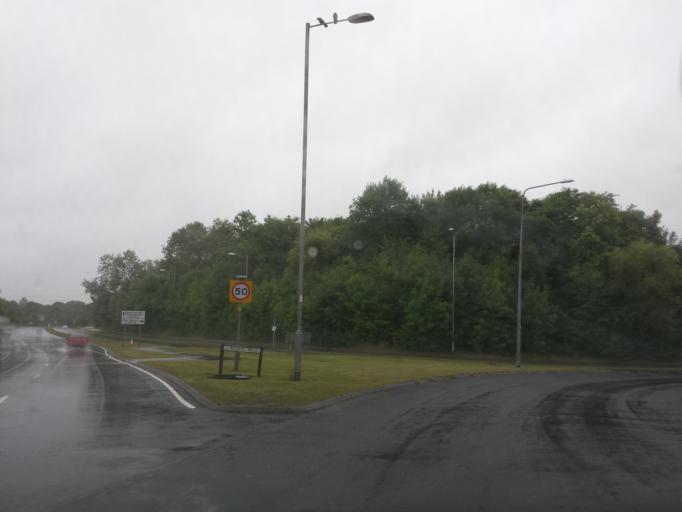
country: GB
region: England
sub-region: Warwickshire
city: Warwick
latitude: 52.3074
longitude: -1.5728
